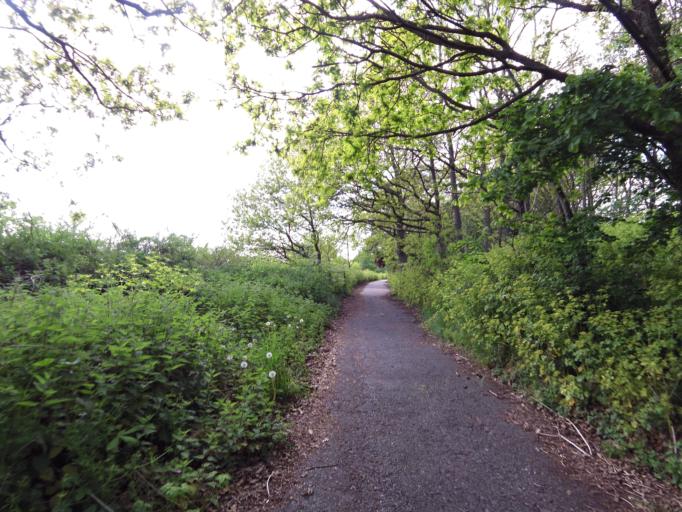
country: GB
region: England
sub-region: Suffolk
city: Beccles
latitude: 52.4461
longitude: 1.6236
